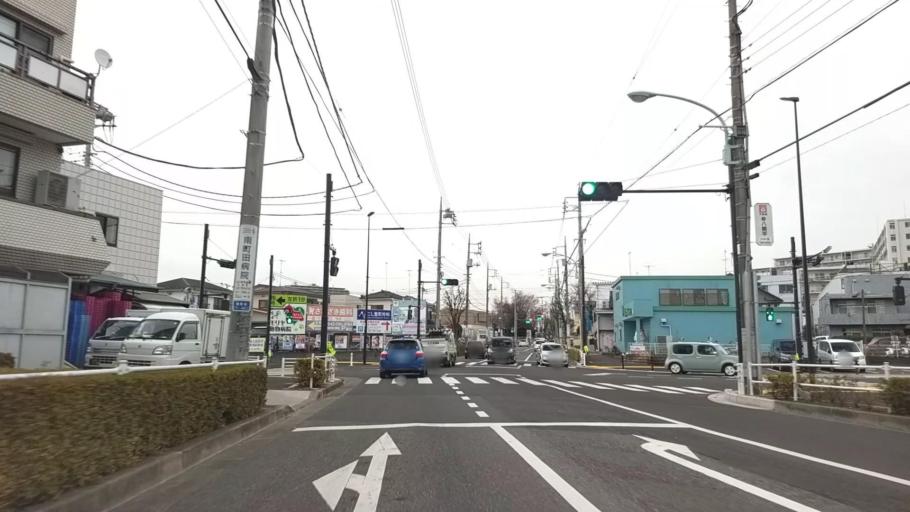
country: JP
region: Tokyo
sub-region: Machida-shi
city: Machida
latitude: 35.5185
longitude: 139.4640
